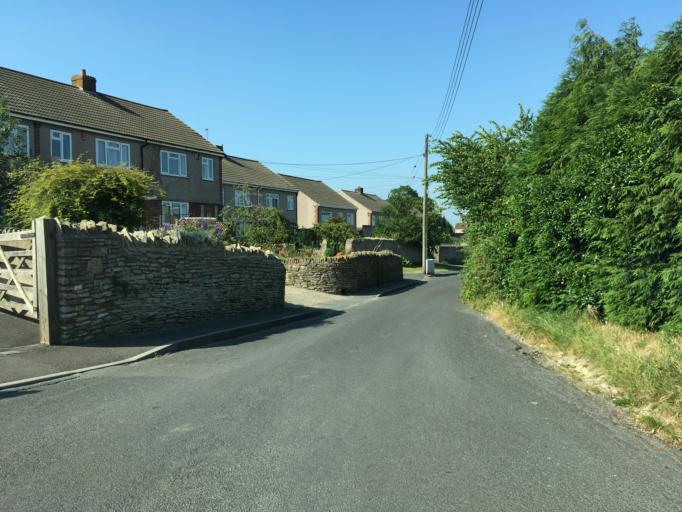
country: GB
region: England
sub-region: South Gloucestershire
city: Stoke Gifford
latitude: 51.5174
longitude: -2.5379
